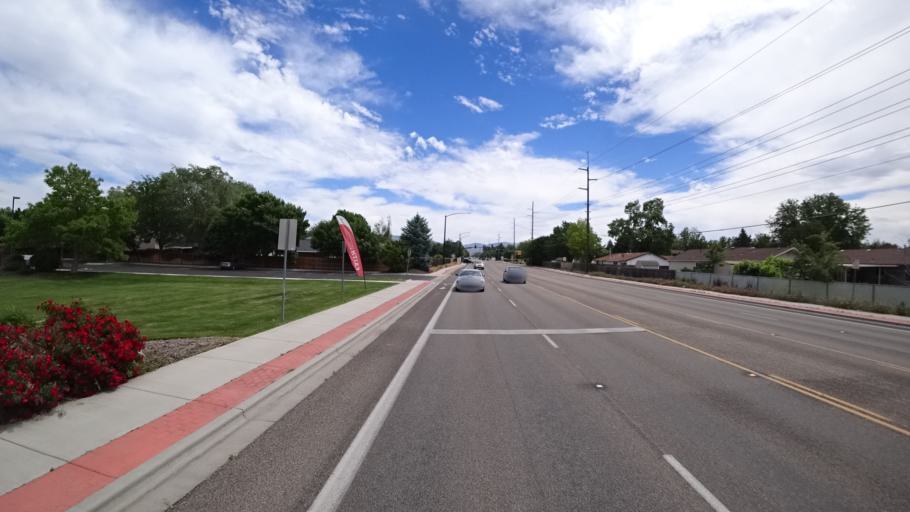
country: US
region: Idaho
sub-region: Ada County
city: Garden City
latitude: 43.6341
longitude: -116.3062
